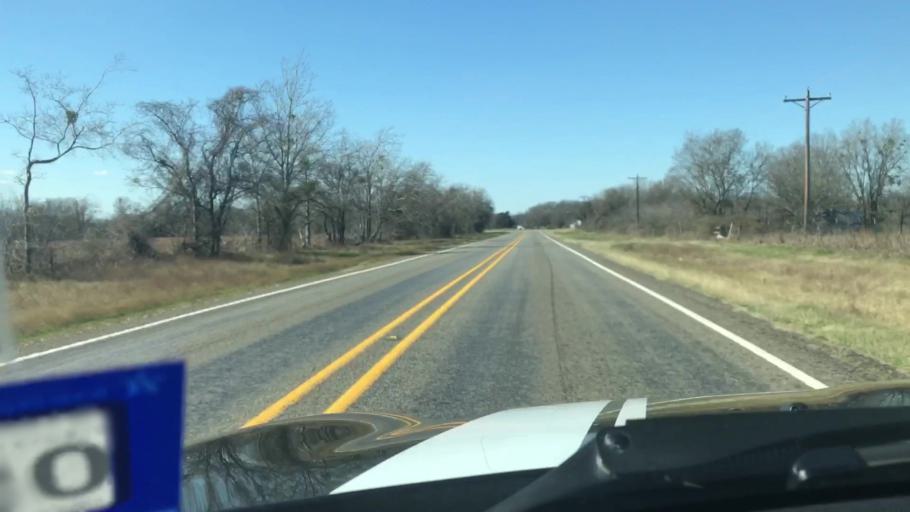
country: US
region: Texas
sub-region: Robertson County
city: Calvert
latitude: 30.8853
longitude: -96.7796
